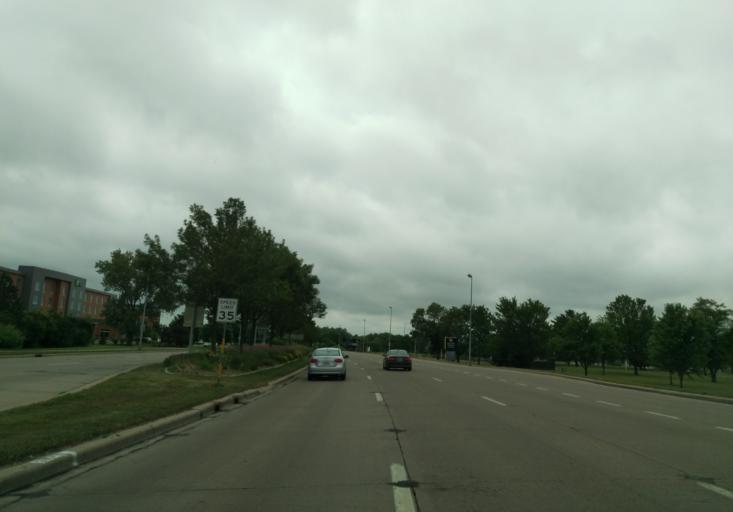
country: US
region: Wisconsin
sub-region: Dane County
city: Madison
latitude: 43.0500
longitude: -89.3775
